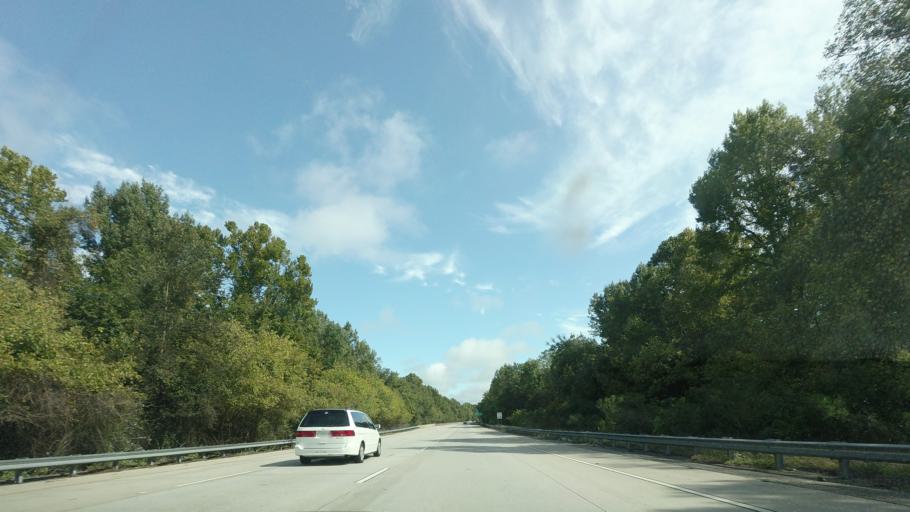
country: US
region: Georgia
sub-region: Bibb County
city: Macon
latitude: 32.7618
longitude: -83.7046
